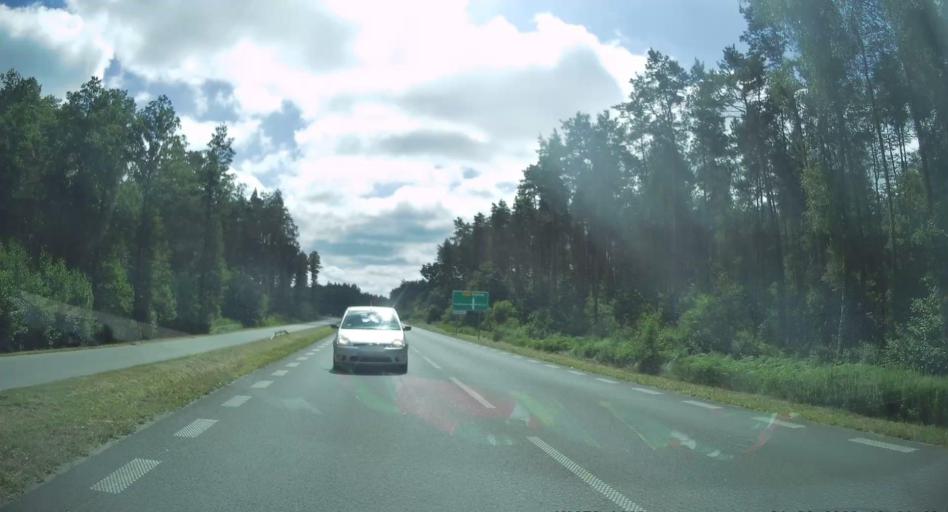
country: PL
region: Subcarpathian Voivodeship
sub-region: Powiat mielecki
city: Mielec
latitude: 50.3183
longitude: 21.5000
